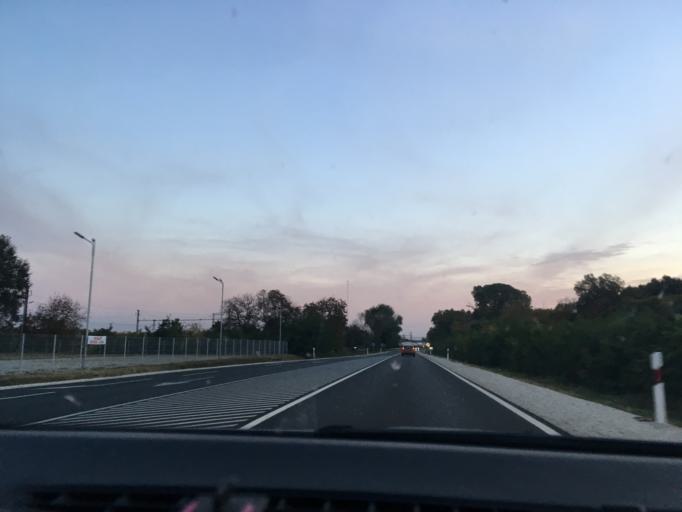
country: HU
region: Hajdu-Bihar
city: Debrecen
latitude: 47.5862
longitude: 21.6548
